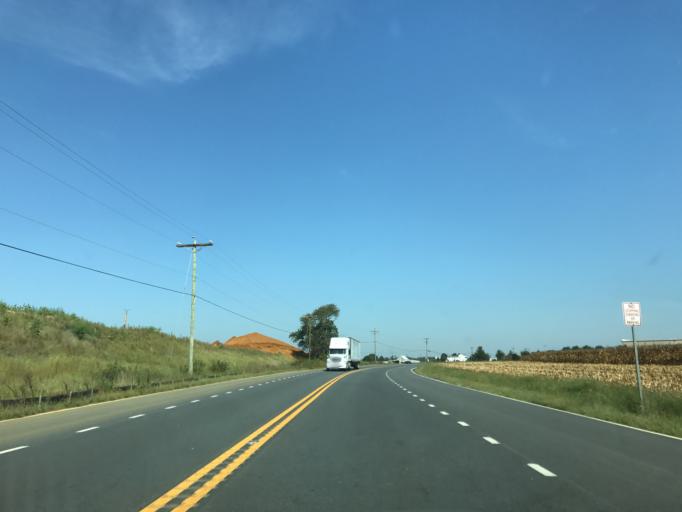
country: US
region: Delaware
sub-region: New Castle County
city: Middletown
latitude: 39.4327
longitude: -75.7587
